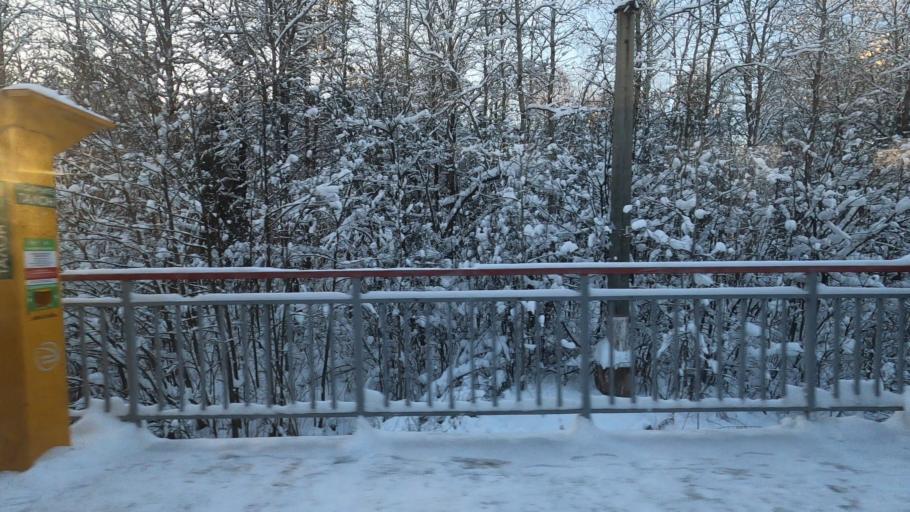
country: RU
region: Moskovskaya
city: Novo-Nikol'skoye
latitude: 56.6394
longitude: 37.5617
